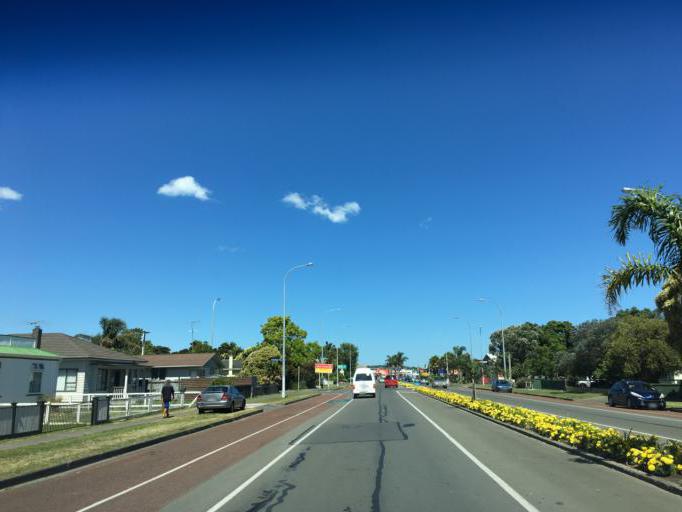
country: NZ
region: Gisborne
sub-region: Gisborne District
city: Gisborne
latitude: -38.6570
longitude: 178.0118
